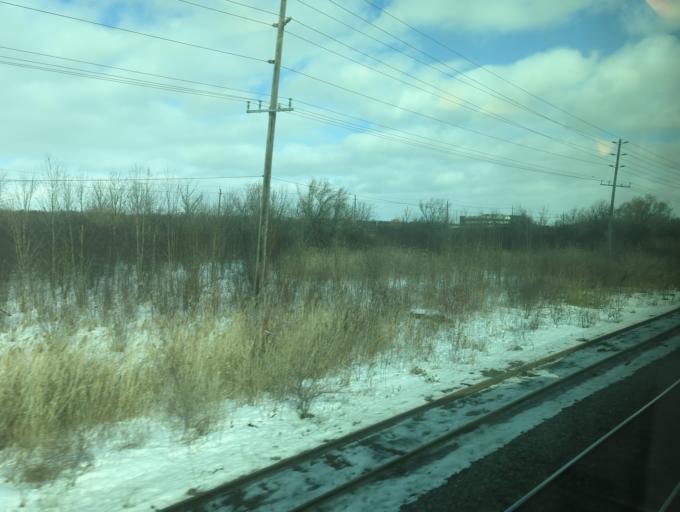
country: CA
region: Ontario
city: Oakville
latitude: 43.4604
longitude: -79.6773
